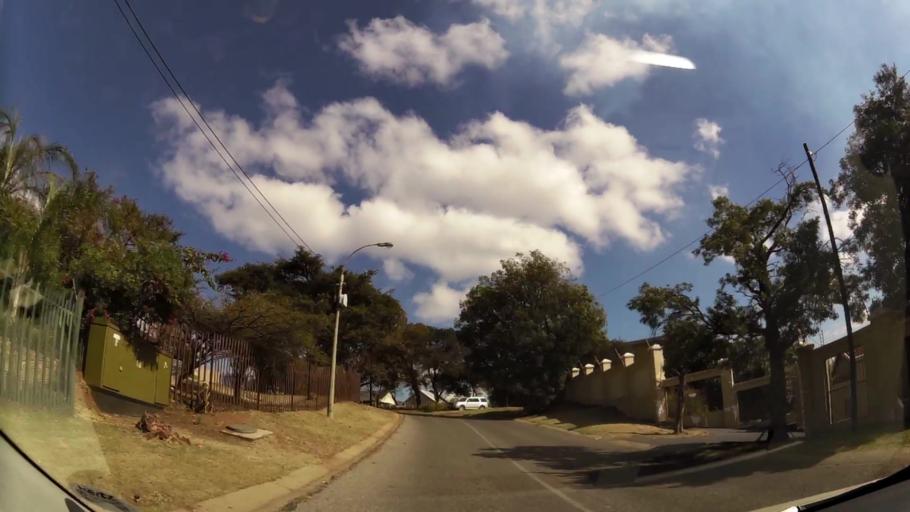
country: ZA
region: Gauteng
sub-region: City of Johannesburg Metropolitan Municipality
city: Roodepoort
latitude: -26.1176
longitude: 27.8393
